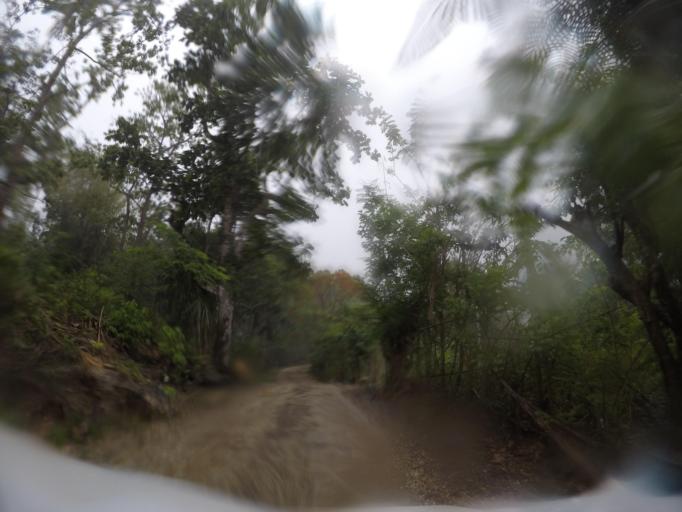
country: TL
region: Baucau
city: Venilale
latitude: -8.6343
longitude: 126.4393
